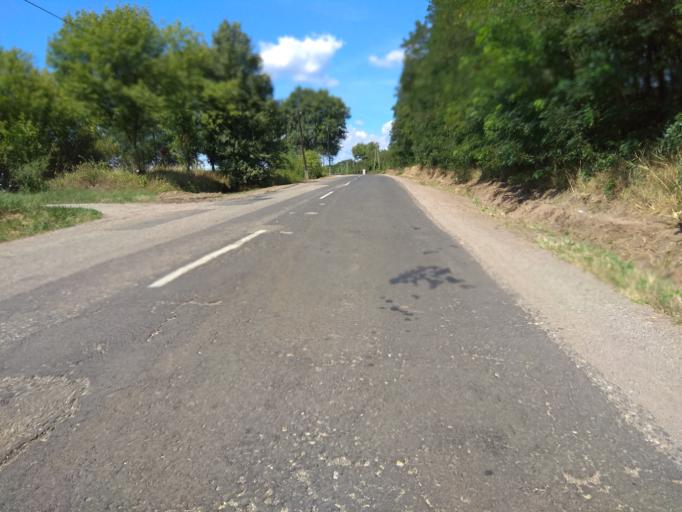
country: HU
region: Borsod-Abauj-Zemplen
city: Kazincbarcika
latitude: 48.2820
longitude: 20.6361
